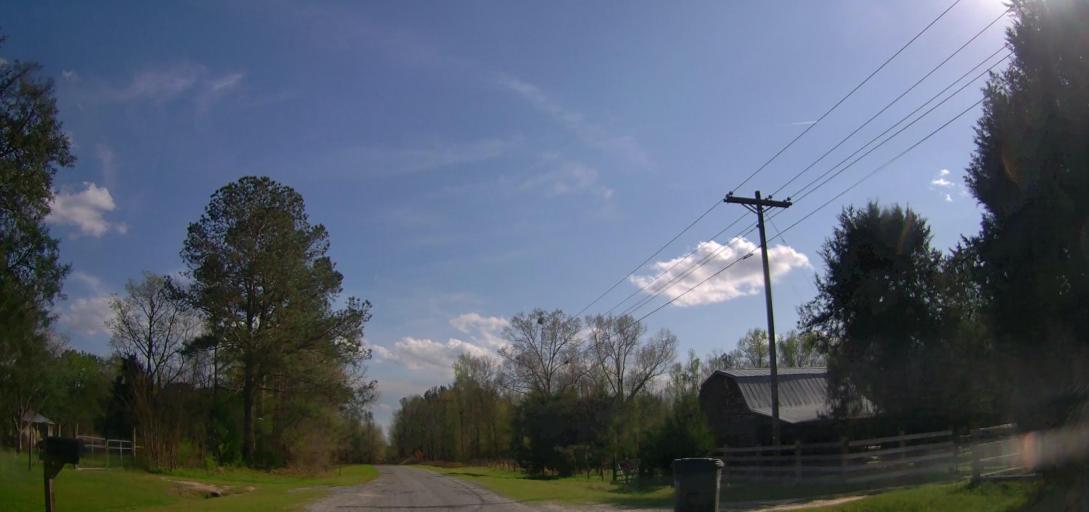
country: US
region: Georgia
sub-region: Baldwin County
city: Hardwick
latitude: 33.0300
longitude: -83.1192
